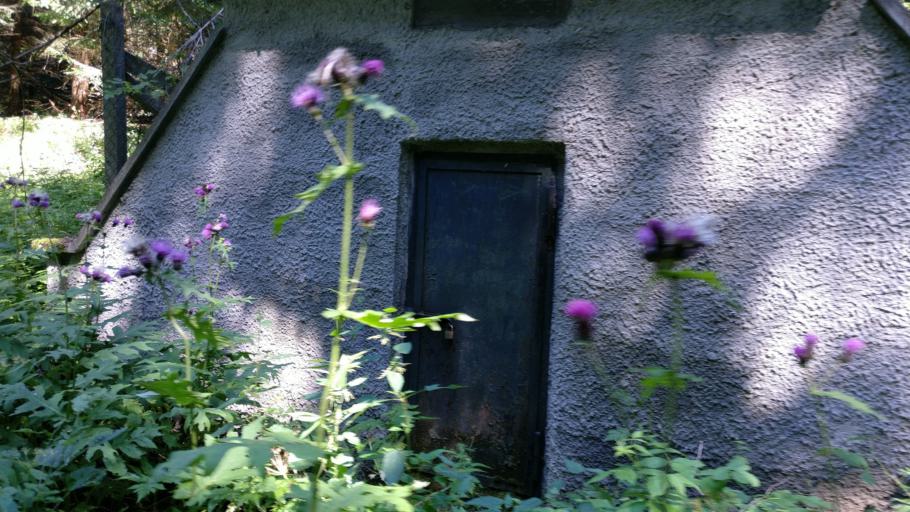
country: IT
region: Trentino-Alto Adige
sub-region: Provincia di Trento
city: Ruffre
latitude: 46.4343
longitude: 11.1889
